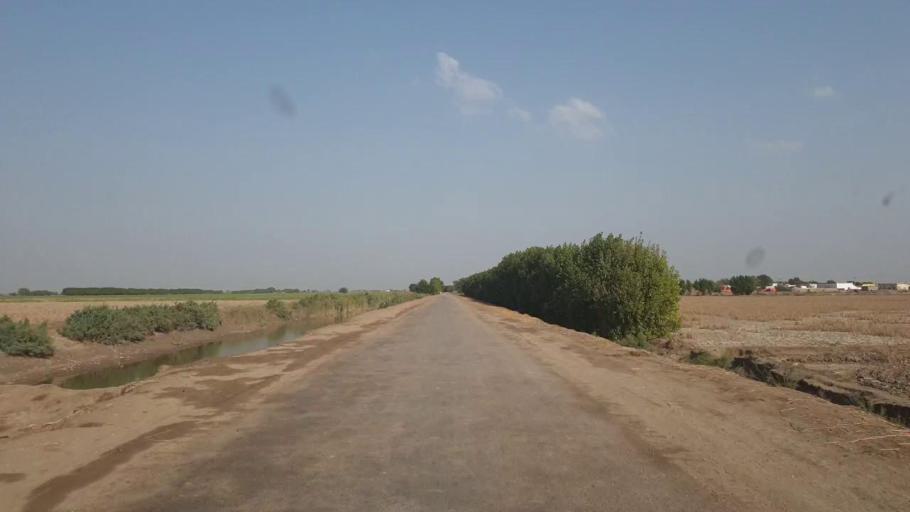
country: PK
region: Sindh
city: Kario
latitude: 24.5823
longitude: 68.5379
